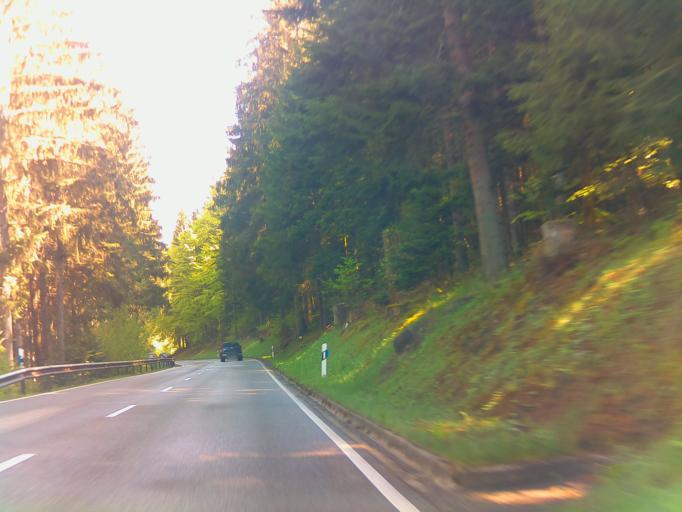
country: DE
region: Baden-Wuerttemberg
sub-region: Karlsruhe Region
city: Bad Wildbad
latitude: 48.7318
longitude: 8.5738
